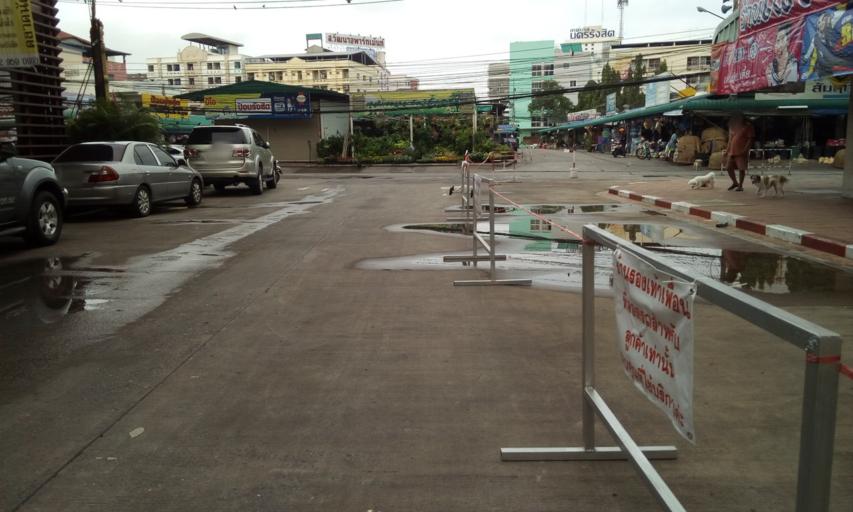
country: TH
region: Phra Nakhon Si Ayutthaya
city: Ban Bang Kadi Pathum Thani
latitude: 13.9869
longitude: 100.6127
